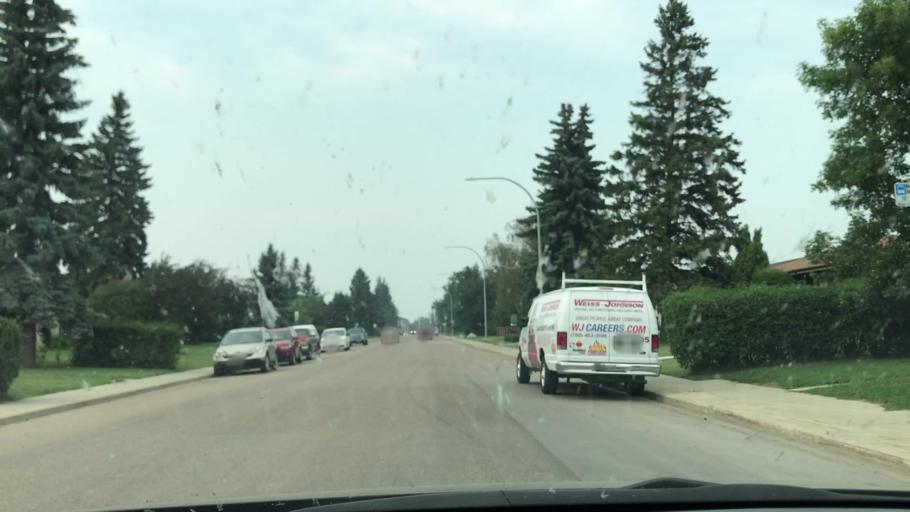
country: CA
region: Alberta
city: St. Albert
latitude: 53.5948
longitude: -113.5535
